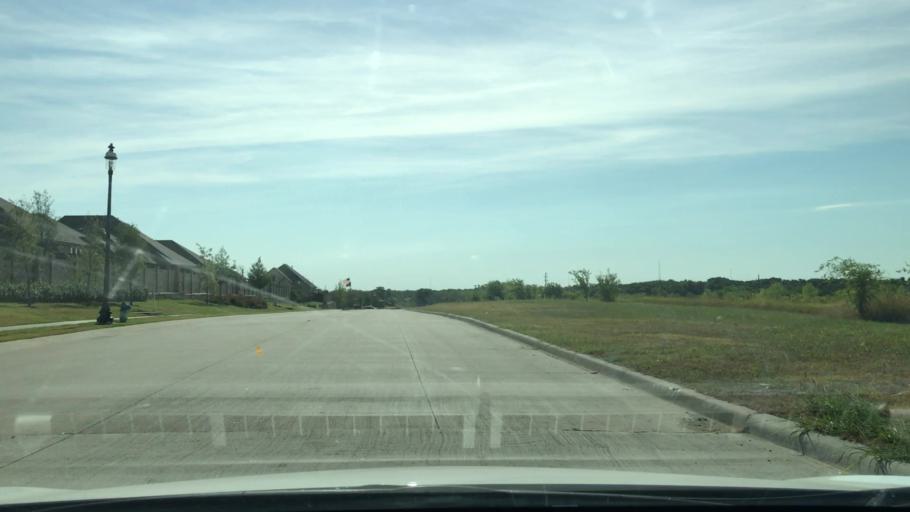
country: US
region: Texas
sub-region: Collin County
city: McKinney
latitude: 33.2401
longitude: -96.6532
